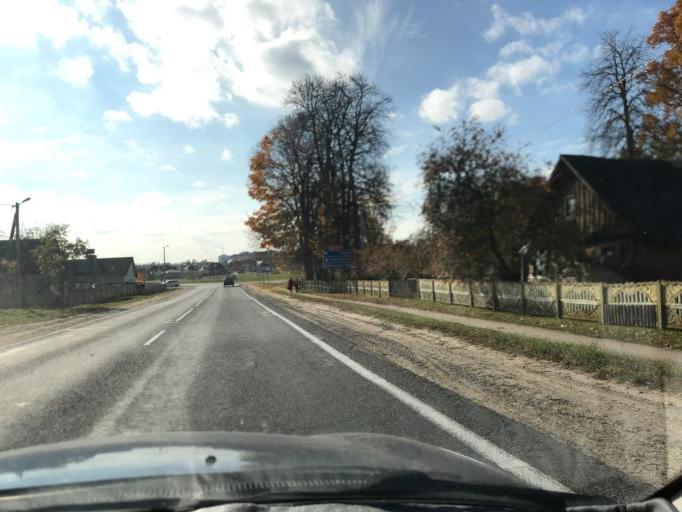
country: BY
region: Grodnenskaya
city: Voranava
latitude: 54.1584
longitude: 25.3264
